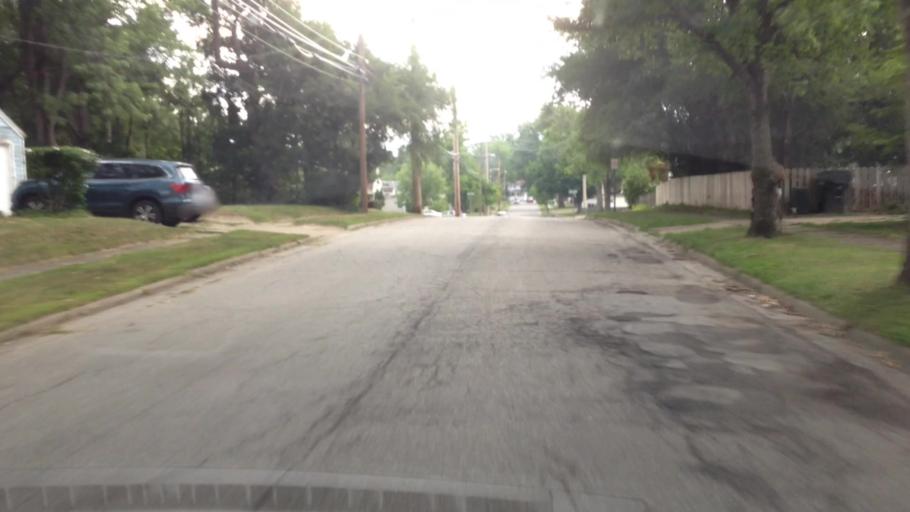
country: US
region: Ohio
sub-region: Summit County
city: Cuyahoga Falls
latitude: 41.1404
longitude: -81.4996
